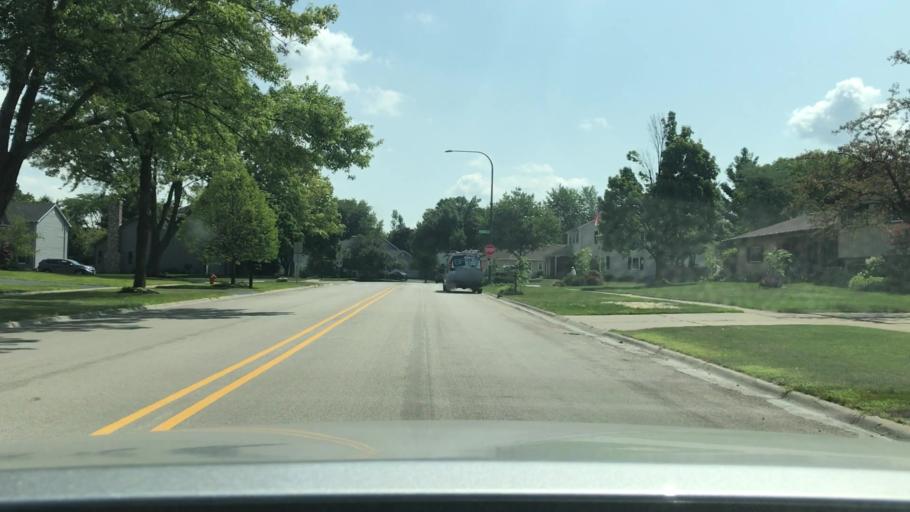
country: US
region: Illinois
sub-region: DuPage County
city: Naperville
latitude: 41.7416
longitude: -88.1092
